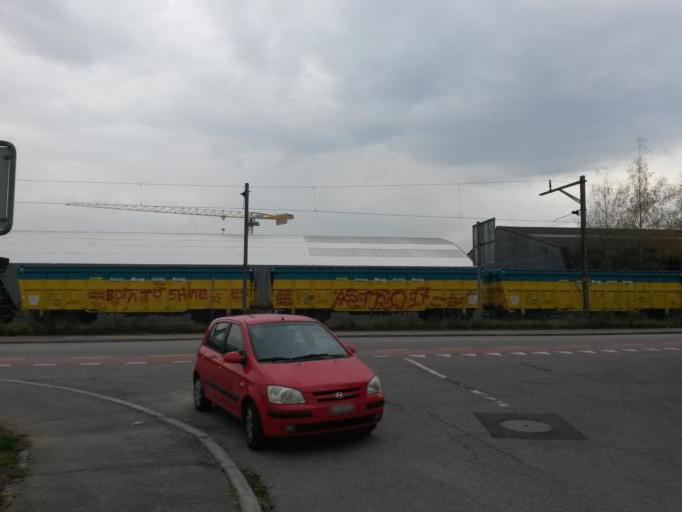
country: CH
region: Solothurn
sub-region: Bezirk Wasseramt
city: Luterbach
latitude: 47.2191
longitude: 7.5850
